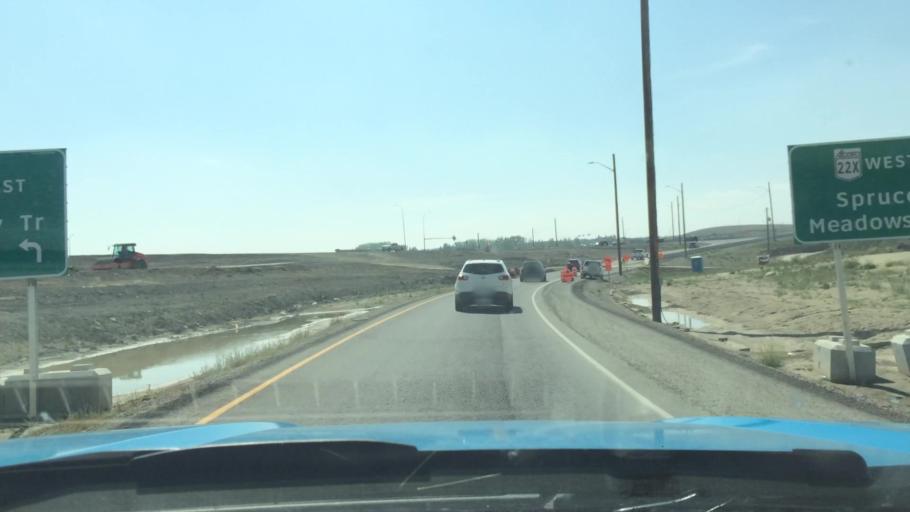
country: CA
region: Alberta
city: Calgary
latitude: 50.8943
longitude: -114.0596
